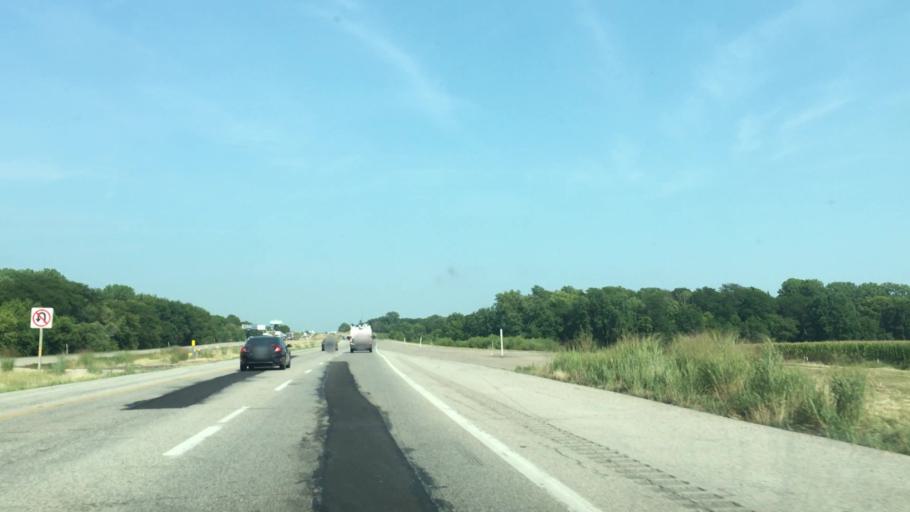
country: US
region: Iowa
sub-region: Cedar County
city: Tipton
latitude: 41.6456
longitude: -91.1412
